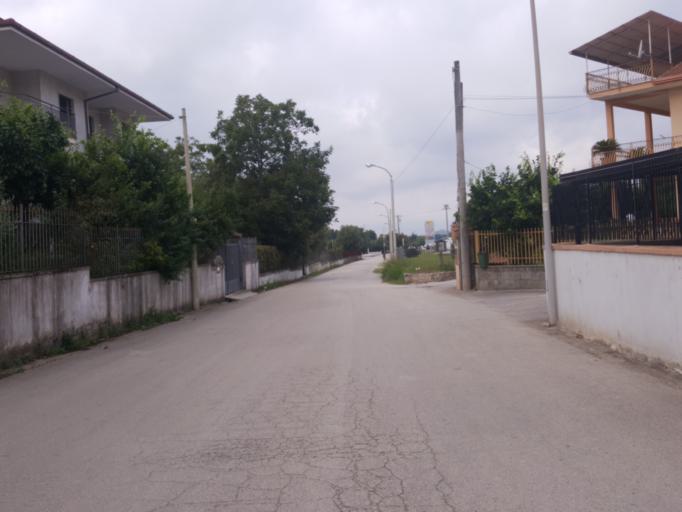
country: IT
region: Campania
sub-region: Provincia di Caserta
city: Pignataro Maggiore
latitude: 41.1891
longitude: 14.1672
